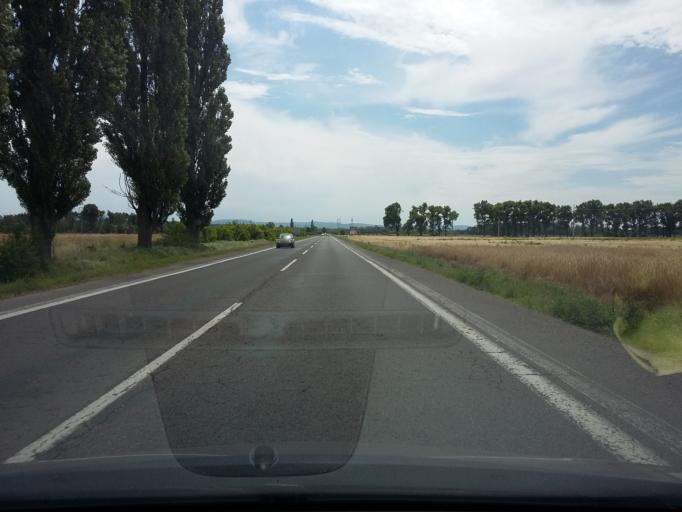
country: SK
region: Bratislavsky
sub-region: Okres Malacky
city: Malacky
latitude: 48.4960
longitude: 17.0046
